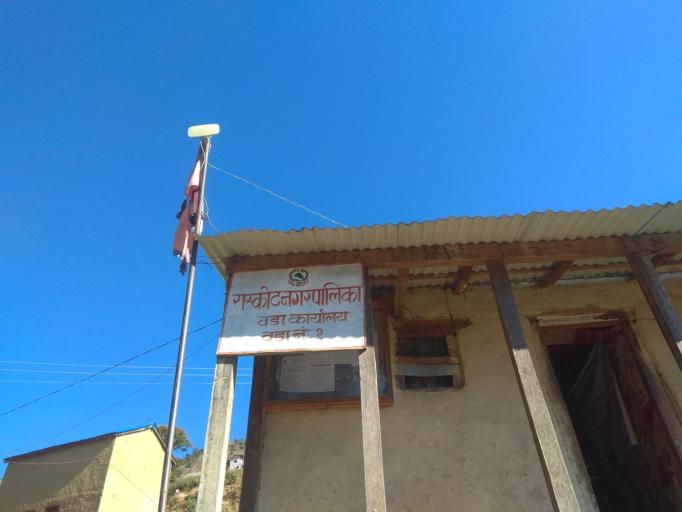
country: NP
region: Far Western
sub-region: Seti Zone
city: Achham
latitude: 29.2610
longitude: 81.6120
